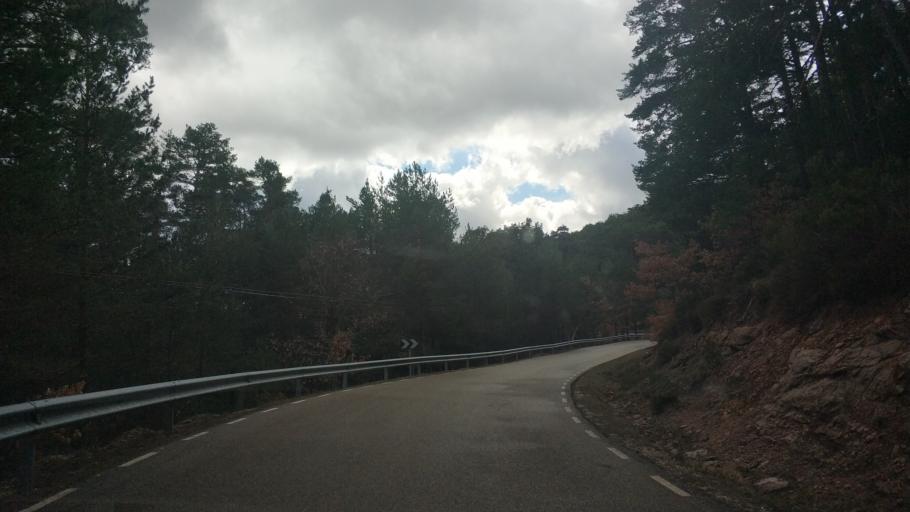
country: ES
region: Castille and Leon
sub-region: Provincia de Burgos
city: Quintanar de la Sierra
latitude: 42.0113
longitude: -3.0197
